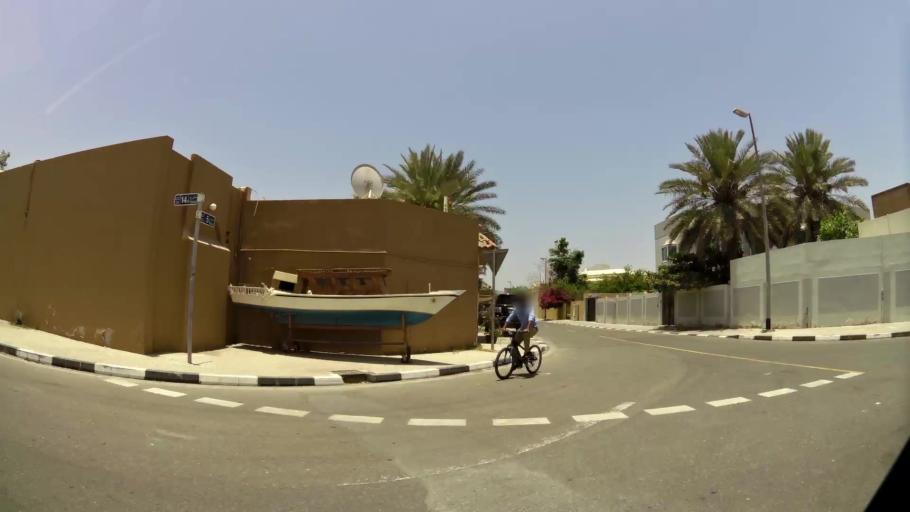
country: AE
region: Ash Shariqah
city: Sharjah
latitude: 25.2432
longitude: 55.2861
